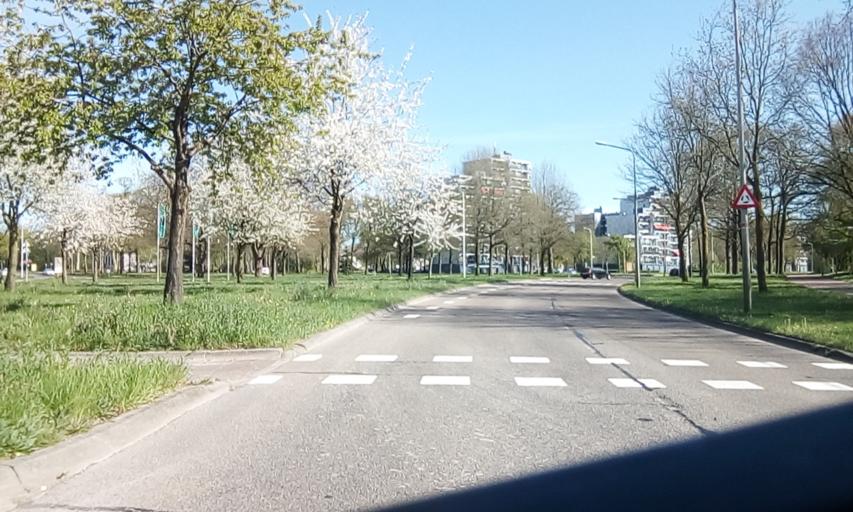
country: NL
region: Gelderland
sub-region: Gemeente Nijmegen
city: Lindenholt
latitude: 51.8174
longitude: 5.8011
